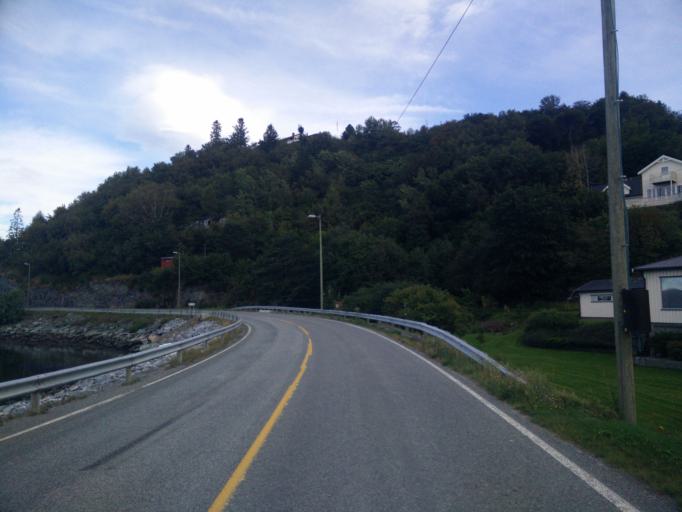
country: NO
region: Sor-Trondelag
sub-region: Melhus
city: Melhus
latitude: 63.3166
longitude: 10.1936
